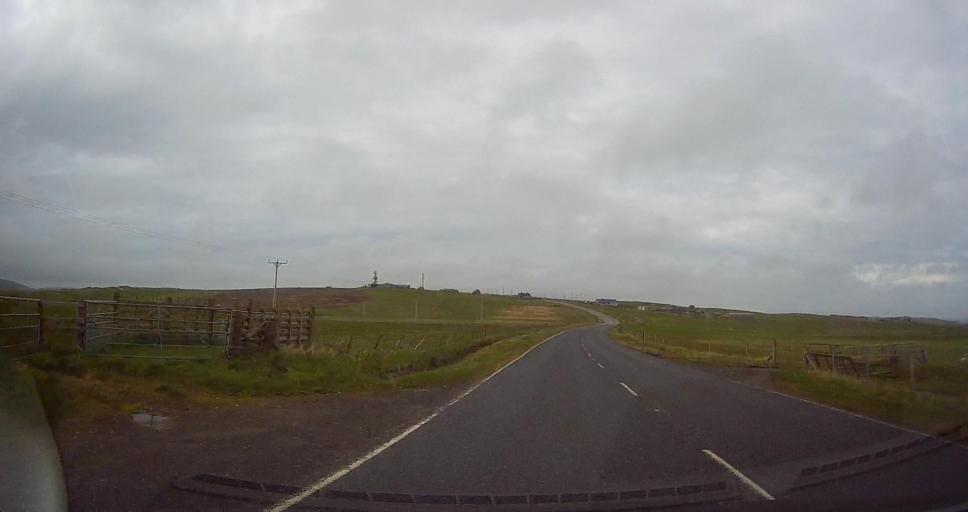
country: GB
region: Scotland
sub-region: Shetland Islands
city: Sandwick
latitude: 59.9057
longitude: -1.3025
